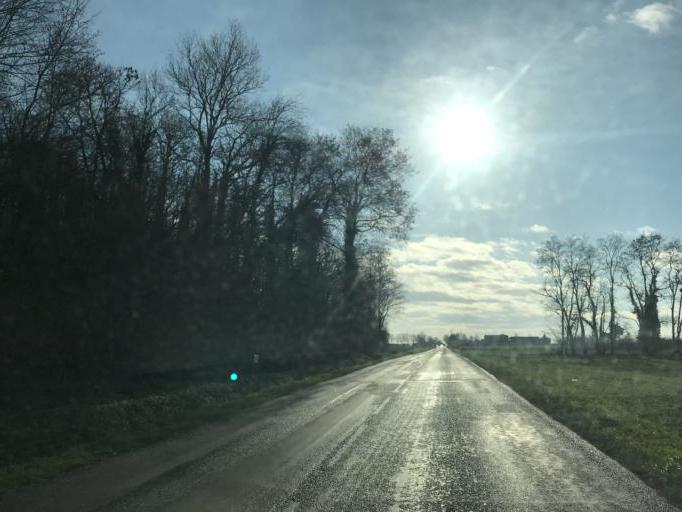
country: FR
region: Rhone-Alpes
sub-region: Departement de l'Ain
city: Civrieux
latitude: 45.9390
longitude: 4.8821
